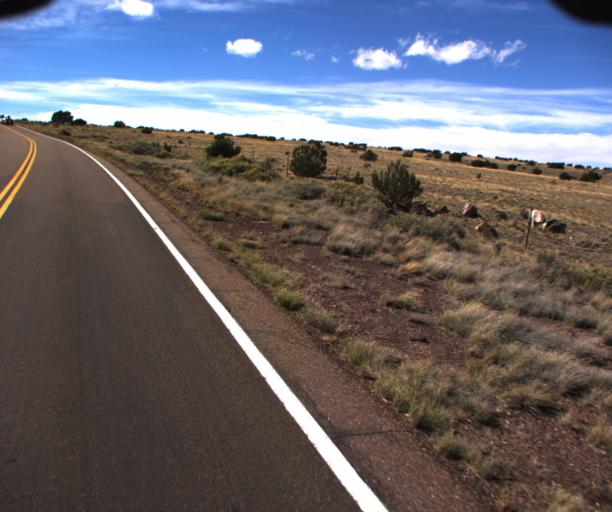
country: US
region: Arizona
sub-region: Apache County
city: Saint Johns
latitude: 34.4998
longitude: -109.4985
